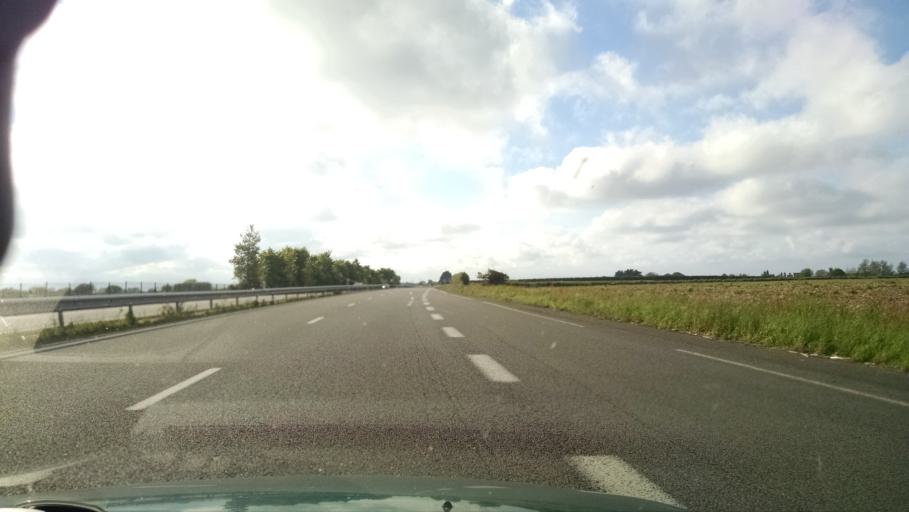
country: FR
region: Brittany
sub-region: Departement du Finistere
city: Taule
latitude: 48.6221
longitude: -3.9035
